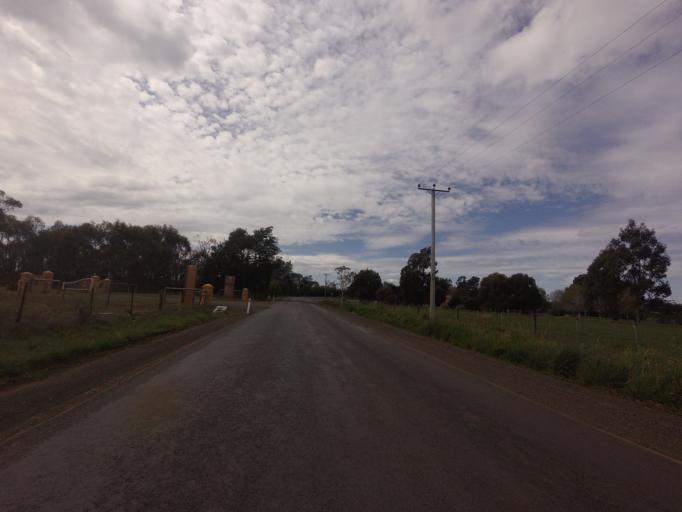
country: AU
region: Tasmania
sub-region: Northern Midlands
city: Longford
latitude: -41.6273
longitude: 147.1559
